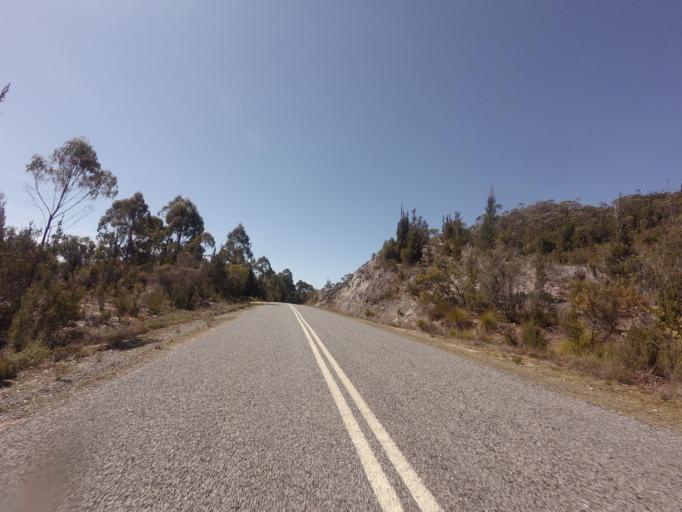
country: AU
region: Tasmania
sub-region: Huon Valley
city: Geeveston
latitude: -42.7937
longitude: 146.3956
